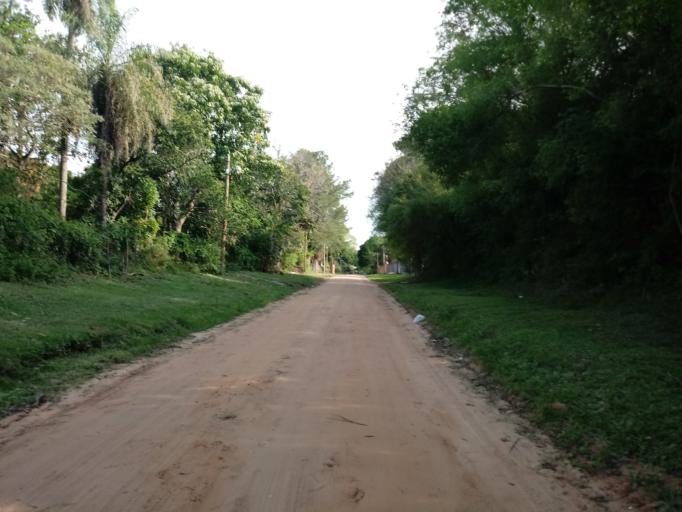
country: AR
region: Corrientes
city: San Luis del Palmar
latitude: -27.4533
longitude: -58.6588
